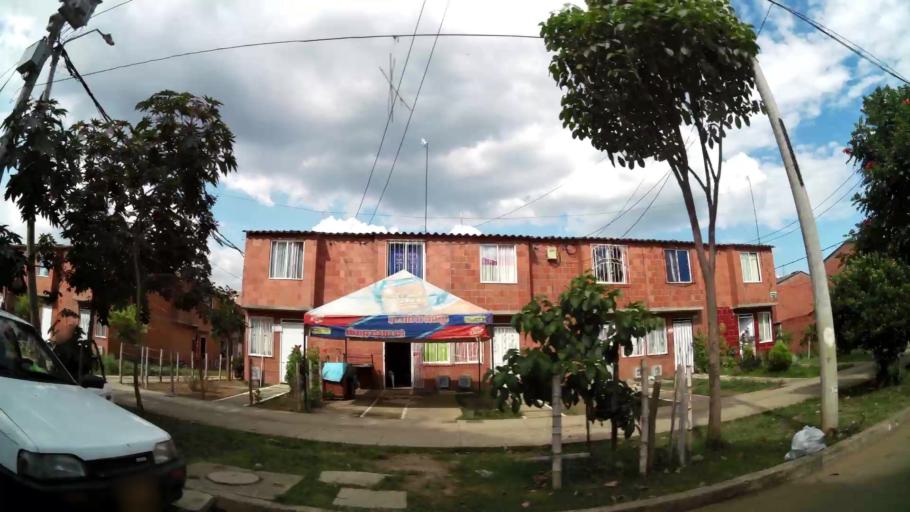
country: CO
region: Valle del Cauca
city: Cali
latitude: 3.3909
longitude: -76.5105
